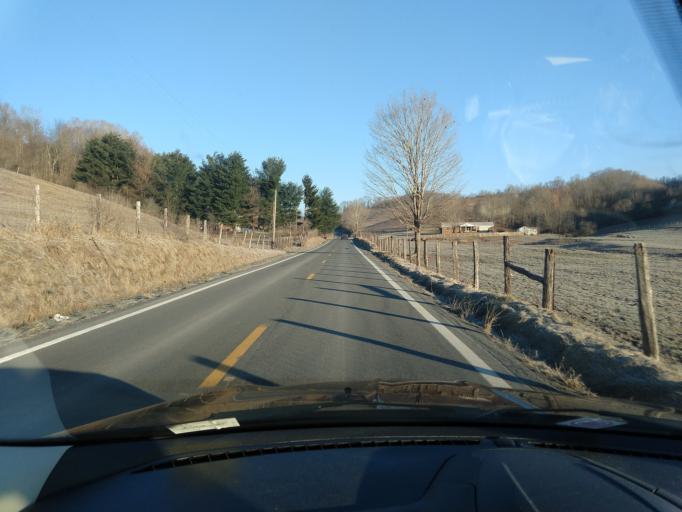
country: US
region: West Virginia
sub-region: Greenbrier County
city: Rainelle
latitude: 37.8659
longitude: -80.7216
